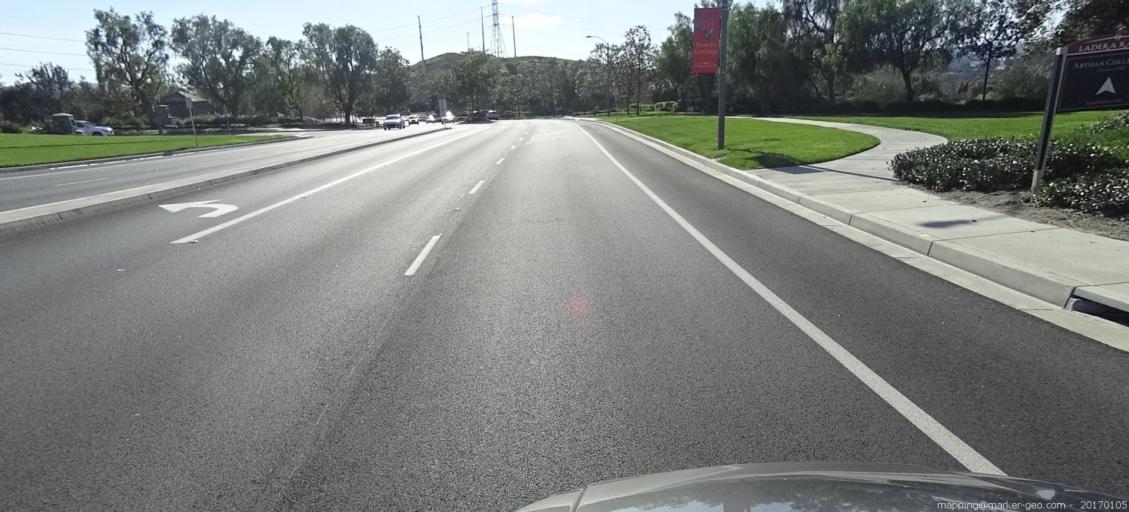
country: US
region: California
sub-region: Orange County
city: Ladera Ranch
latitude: 33.5610
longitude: -117.6438
